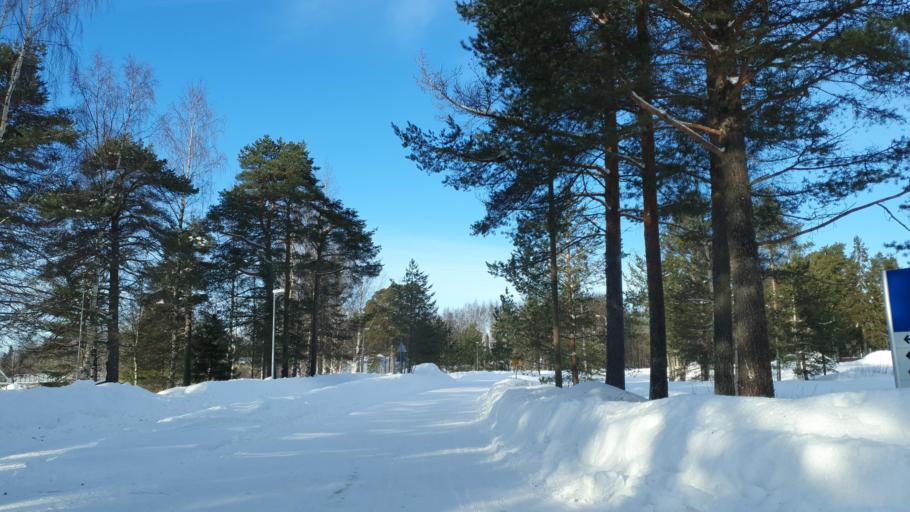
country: FI
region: Northern Ostrobothnia
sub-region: Oulu
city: Haukipudas
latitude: 65.1936
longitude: 25.4131
